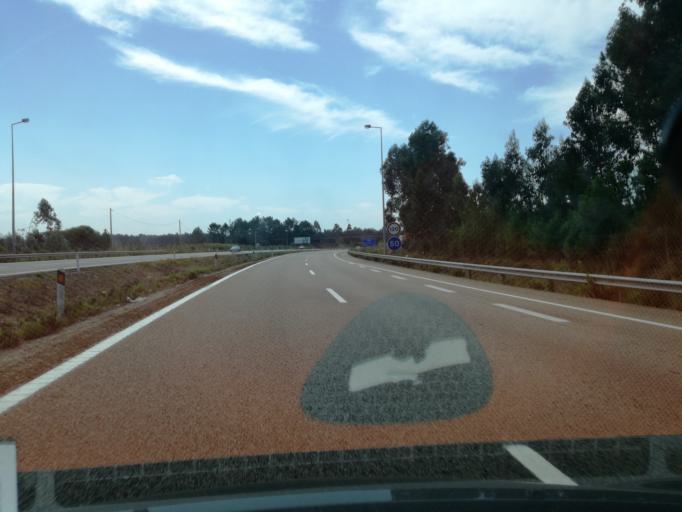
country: PT
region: Porto
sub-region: Povoa de Varzim
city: Pedroso
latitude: 41.4521
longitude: -8.7322
